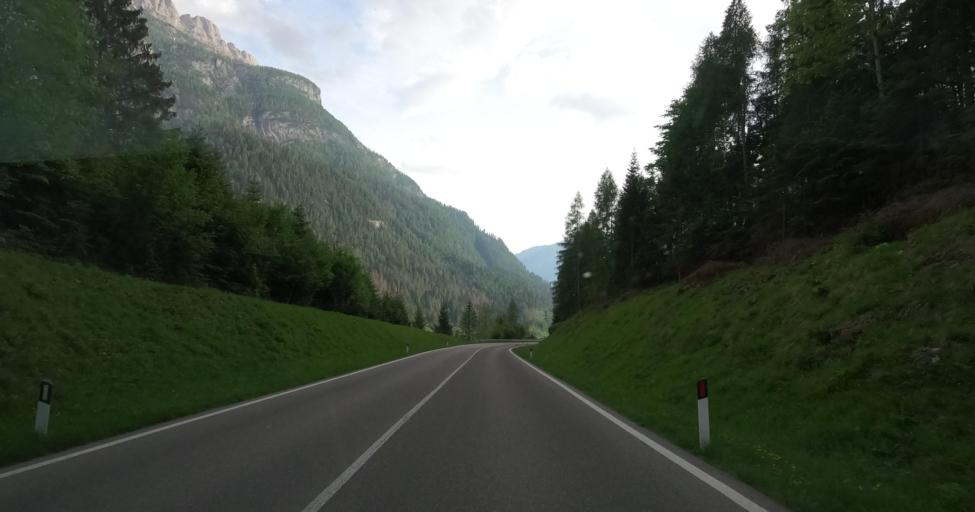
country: IT
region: Veneto
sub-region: Provincia di Belluno
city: Celat-San Tomaso Agordino
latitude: 46.3908
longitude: 11.9981
